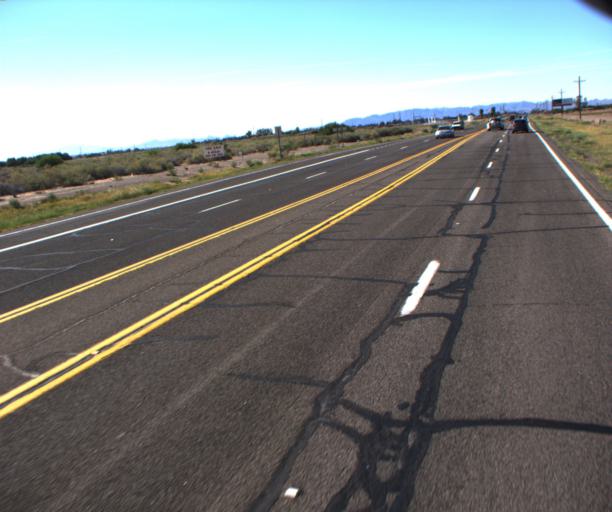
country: US
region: Arizona
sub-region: Mohave County
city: Mohave Valley
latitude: 34.9311
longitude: -114.5980
